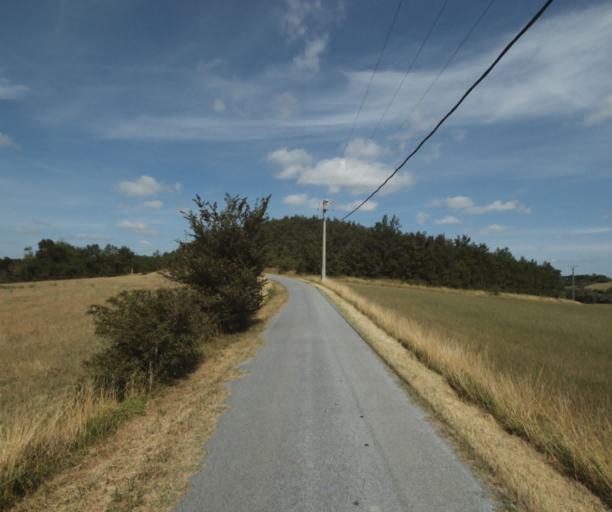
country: FR
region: Midi-Pyrenees
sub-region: Departement du Tarn
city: Dourgne
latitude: 43.4750
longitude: 2.1135
